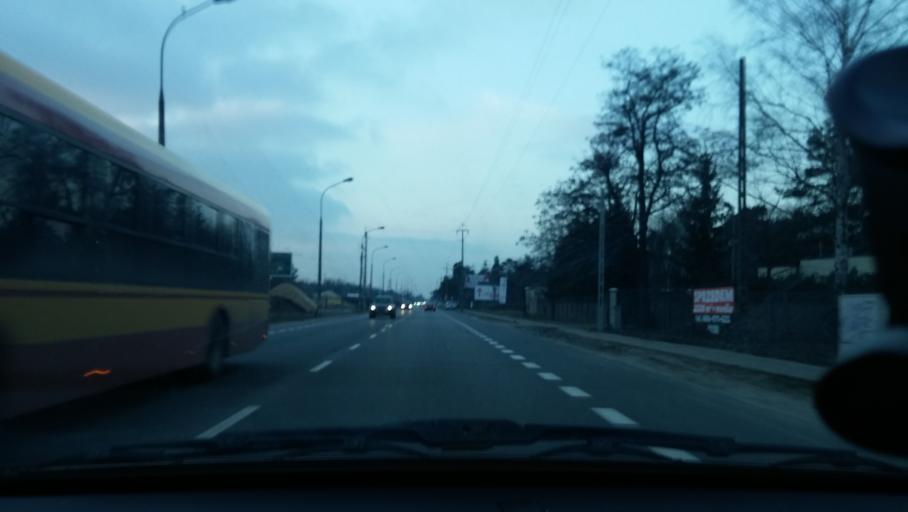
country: PL
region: Masovian Voivodeship
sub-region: Warszawa
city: Wawer
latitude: 52.1894
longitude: 21.1840
